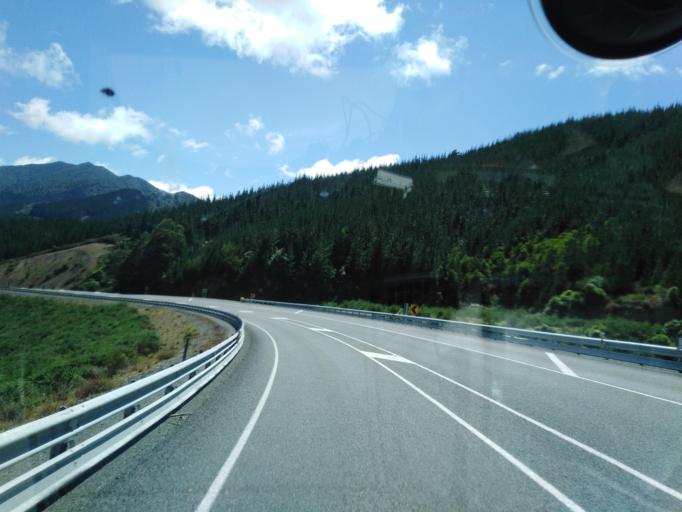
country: NZ
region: Nelson
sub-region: Nelson City
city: Nelson
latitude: -41.1852
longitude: 173.5594
